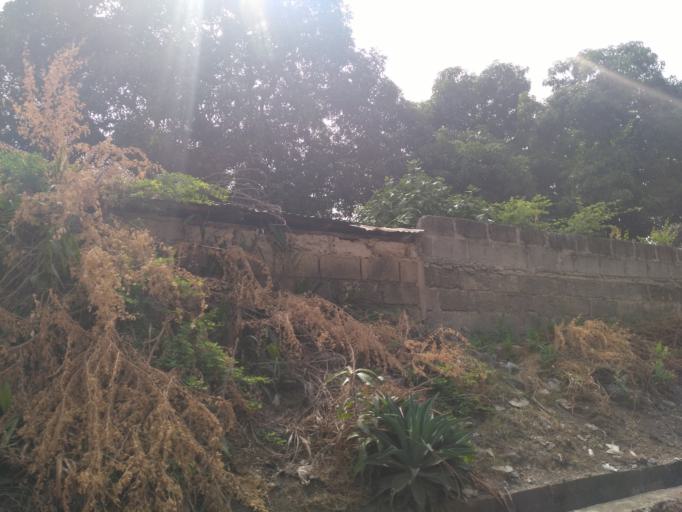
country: GH
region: Ashanti
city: Kumasi
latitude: 6.6763
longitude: -1.6023
